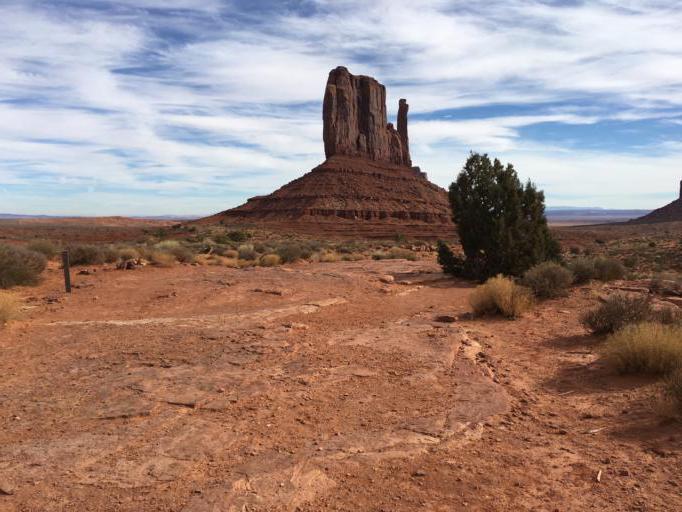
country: US
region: Arizona
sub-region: Navajo County
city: Kayenta
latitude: 36.9899
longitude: -110.1074
